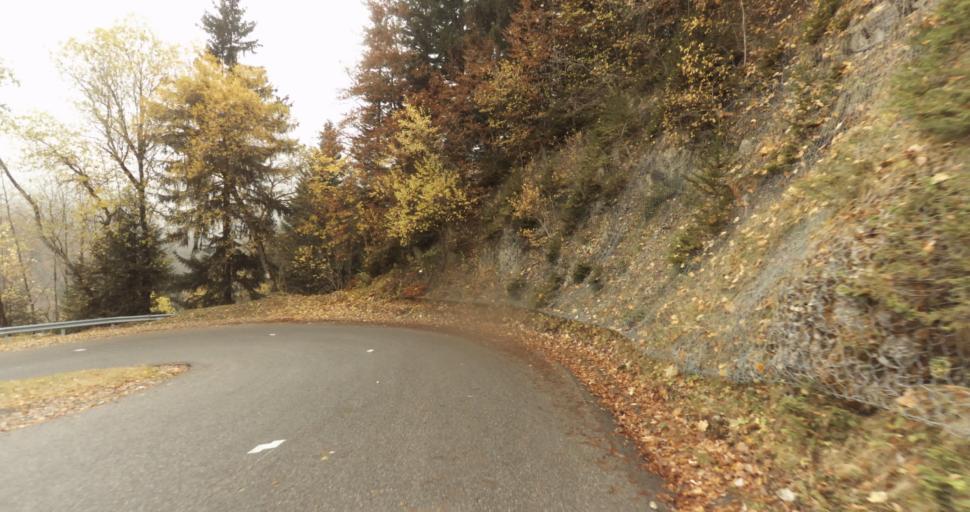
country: FR
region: Rhone-Alpes
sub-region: Departement de la Haute-Savoie
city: Thorens-Glieres
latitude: 45.9666
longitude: 6.2959
